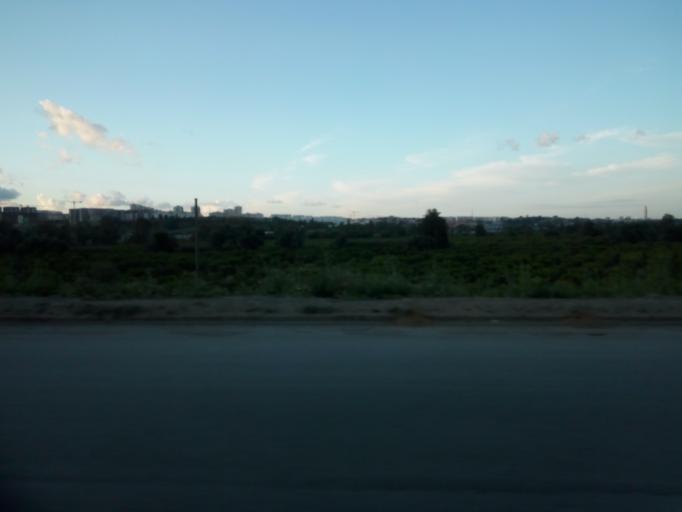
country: DZ
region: Tipaza
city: Baraki
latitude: 36.6774
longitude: 3.0690
